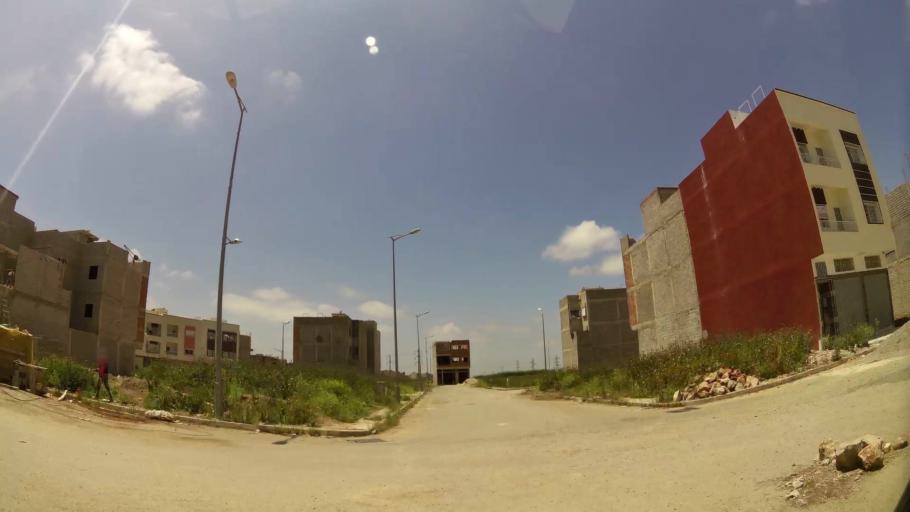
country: MA
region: Fes-Boulemane
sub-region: Fes
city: Fes
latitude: 34.0370
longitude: -5.0566
